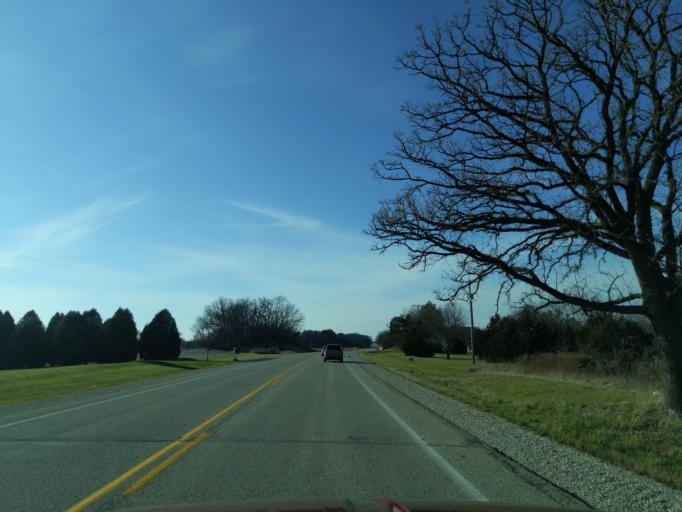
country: US
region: Wisconsin
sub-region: Rock County
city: Milton
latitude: 42.8270
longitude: -88.8815
